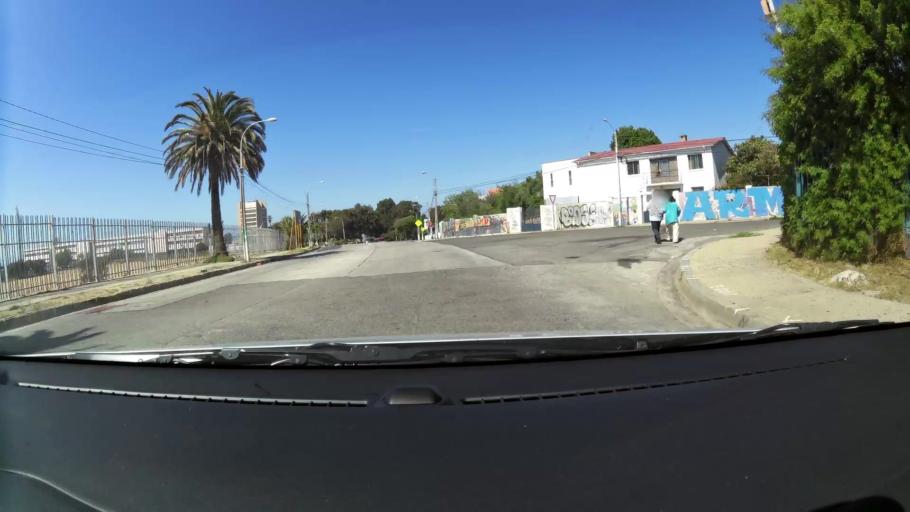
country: CL
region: Valparaiso
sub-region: Provincia de Valparaiso
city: Valparaiso
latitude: -33.0244
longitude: -71.6386
